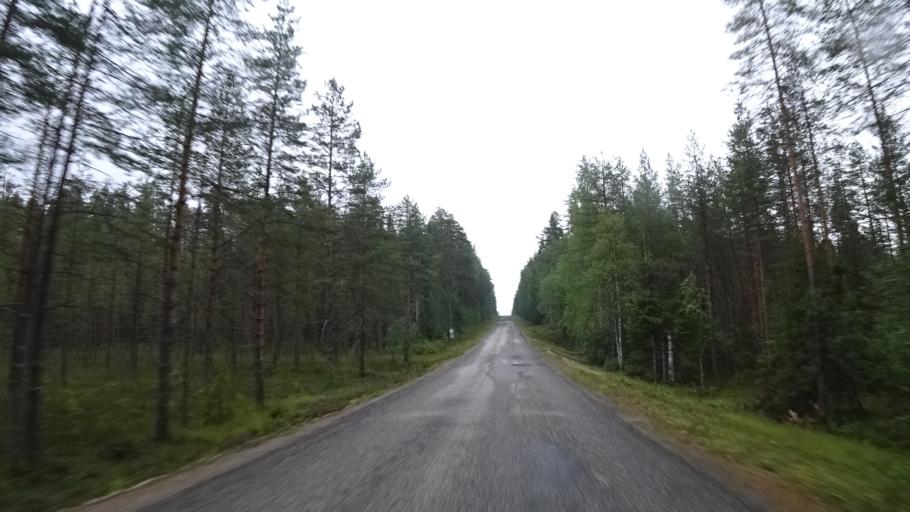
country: FI
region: North Karelia
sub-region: Joensuu
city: Ilomantsi
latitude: 63.2278
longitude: 30.8414
